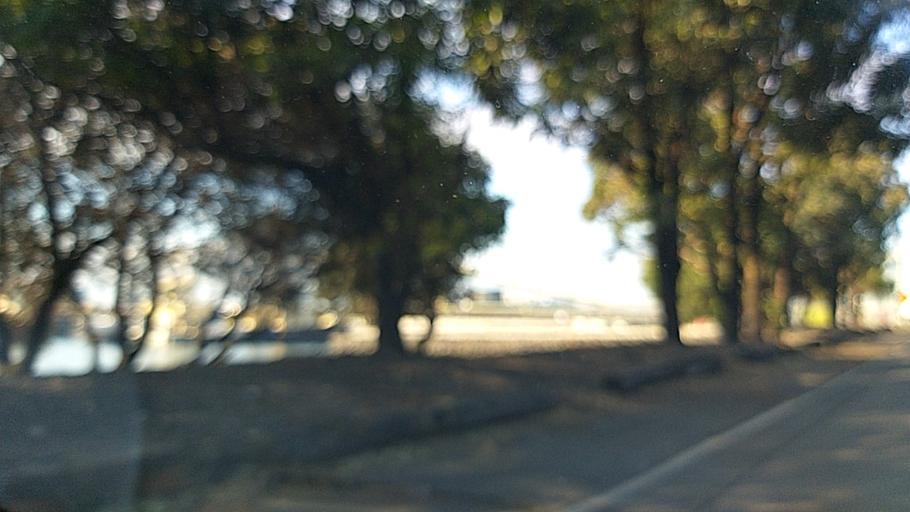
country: AU
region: New South Wales
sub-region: Wollongong
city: Port Kembla
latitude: -34.4670
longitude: 150.9000
